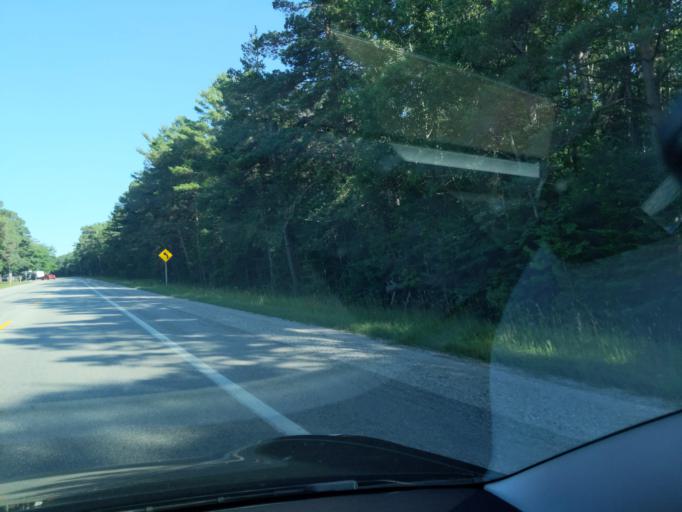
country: US
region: Michigan
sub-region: Mackinac County
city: Saint Ignace
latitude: 45.7516
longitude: -84.6889
